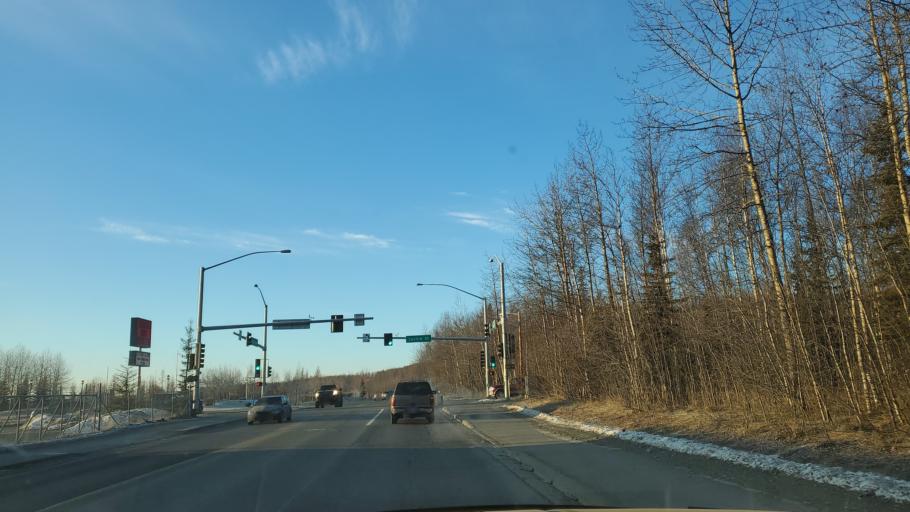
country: US
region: Alaska
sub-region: Matanuska-Susitna Borough
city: Wasilla
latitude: 61.5850
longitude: -149.4496
